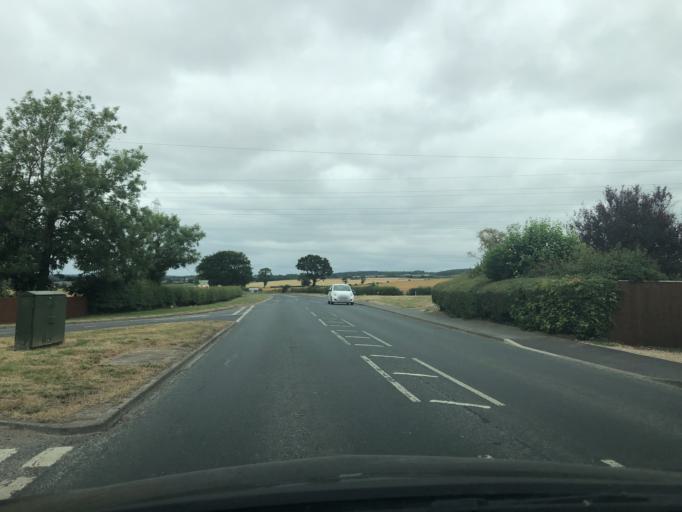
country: GB
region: England
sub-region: North Yorkshire
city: East Ayton
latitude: 54.2450
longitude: -0.4505
